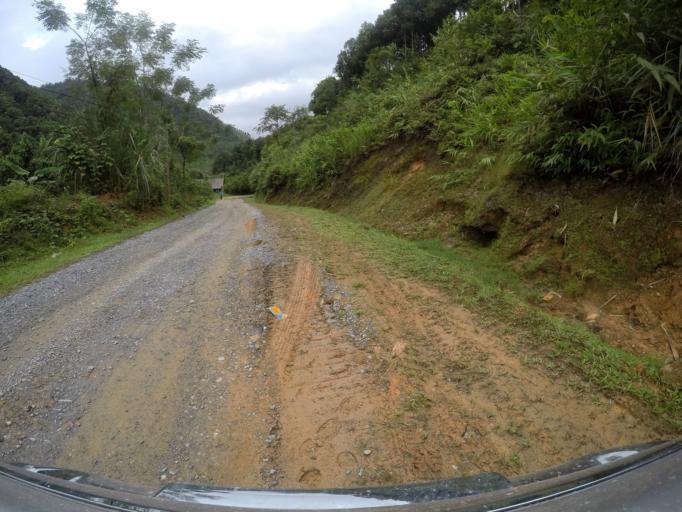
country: VN
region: Yen Bai
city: Co Phuc
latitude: 21.8113
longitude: 104.6306
